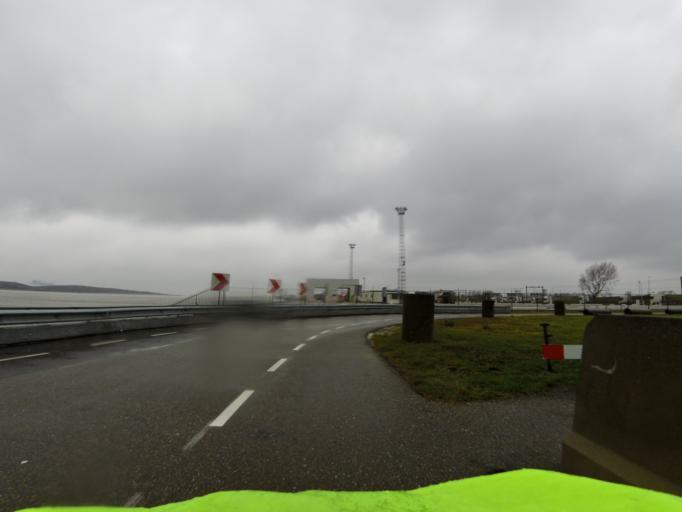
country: NL
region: South Holland
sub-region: Gemeente Rotterdam
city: Hoek van Holland
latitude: 51.9657
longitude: 4.1494
